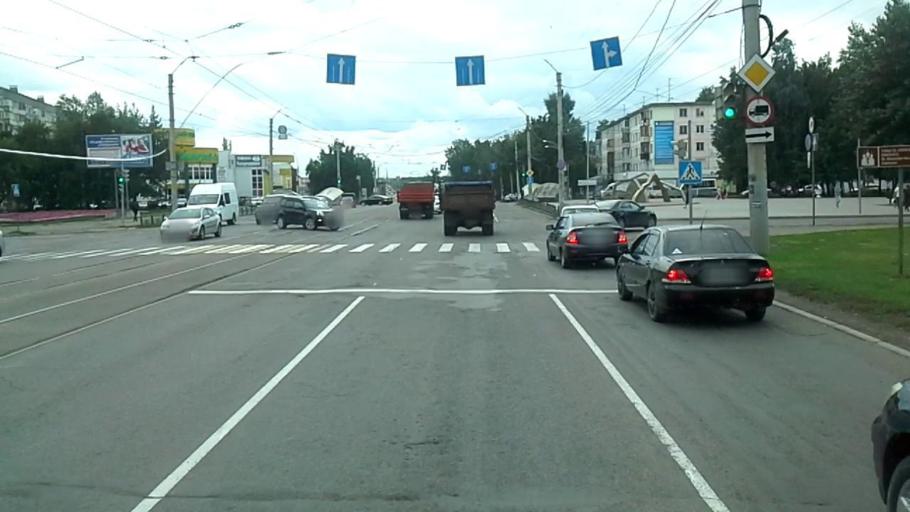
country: RU
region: Altai Krai
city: Biysk
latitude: 52.5420
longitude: 85.2190
